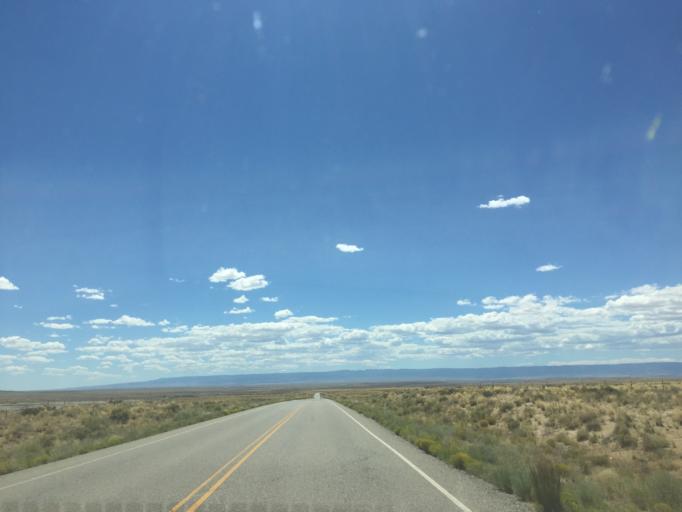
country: US
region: New Mexico
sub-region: San Juan County
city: Upper Fruitland
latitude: 36.4170
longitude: -108.4403
